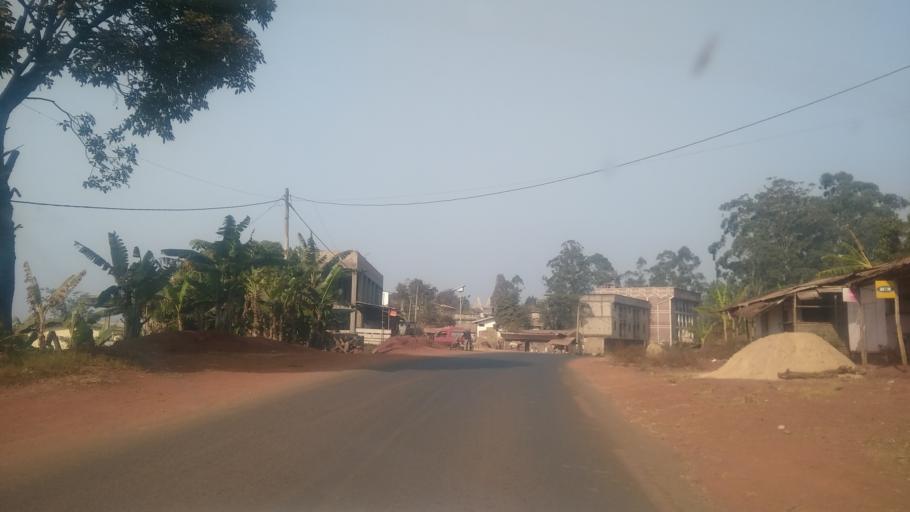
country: CM
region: West
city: Bamendjou
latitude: 5.3331
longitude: 10.3628
